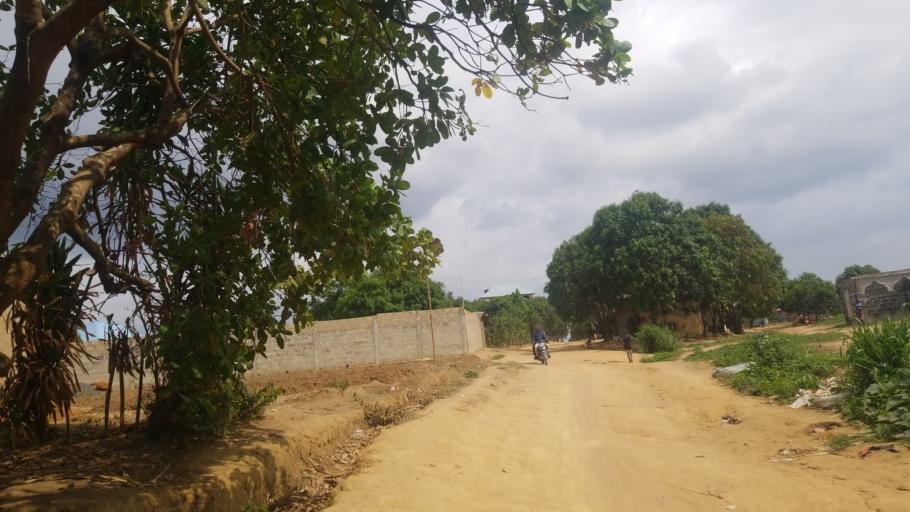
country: SL
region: Western Area
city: Waterloo
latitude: 8.3430
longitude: -13.0528
